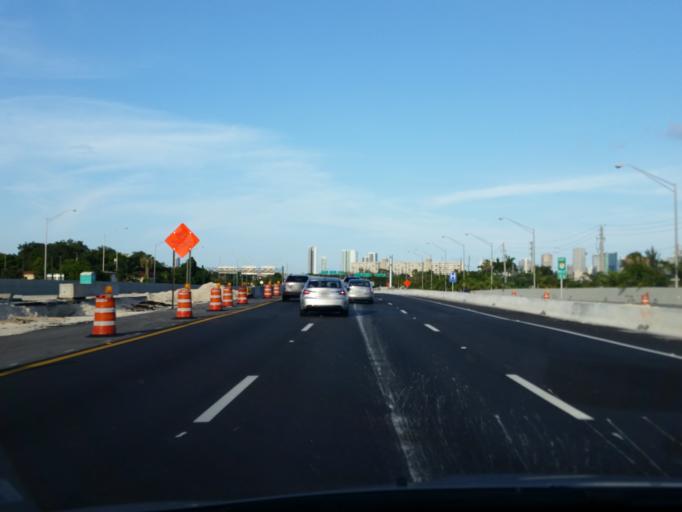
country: US
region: Florida
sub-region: Miami-Dade County
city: Allapattah
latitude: 25.7822
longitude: -80.2285
